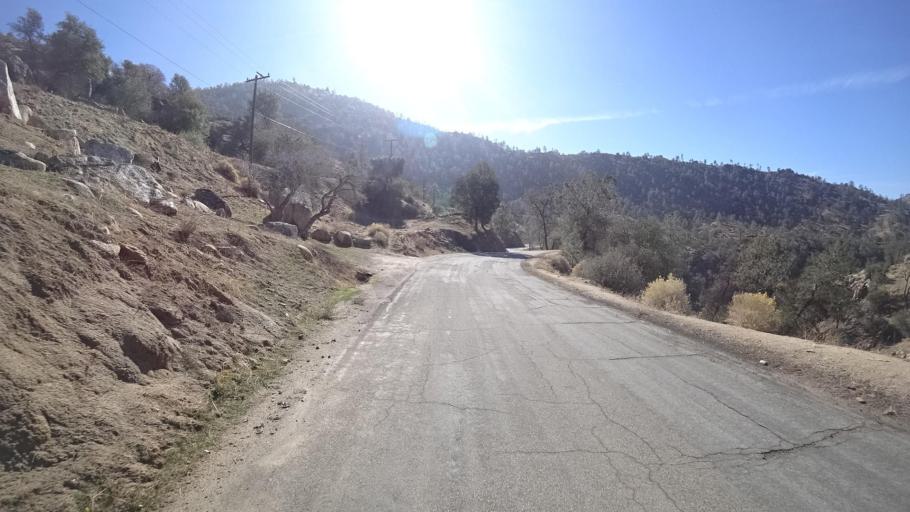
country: US
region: California
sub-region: Kern County
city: Bodfish
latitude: 35.5691
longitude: -118.5668
